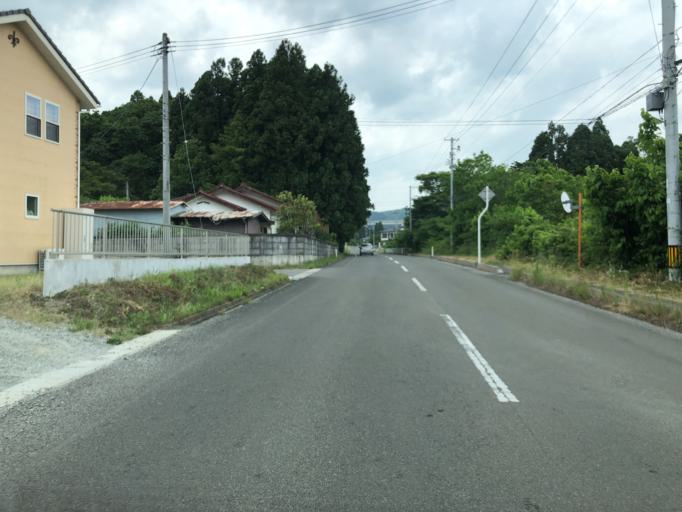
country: JP
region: Miyagi
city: Marumori
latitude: 37.8212
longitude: 140.8833
